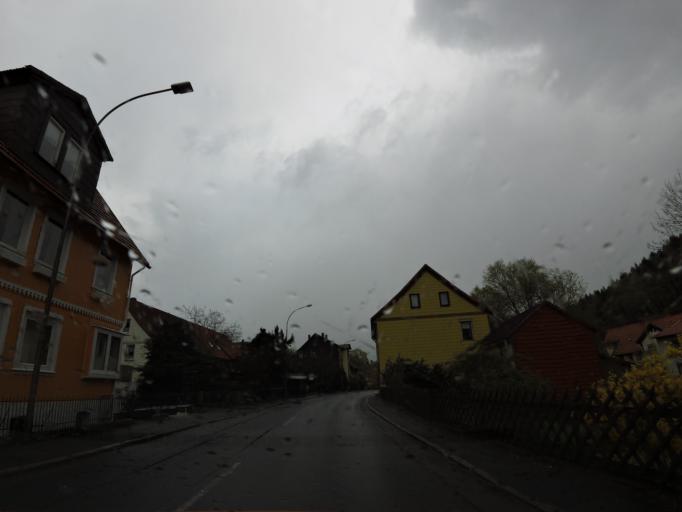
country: DE
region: Lower Saxony
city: Goslar
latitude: 51.8946
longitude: 10.4804
